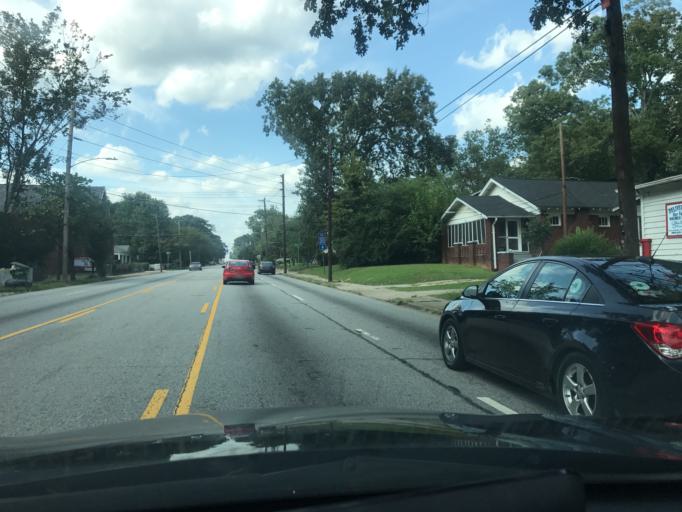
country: US
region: Georgia
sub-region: Fulton County
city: Atlanta
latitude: 33.7352
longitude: -84.3493
